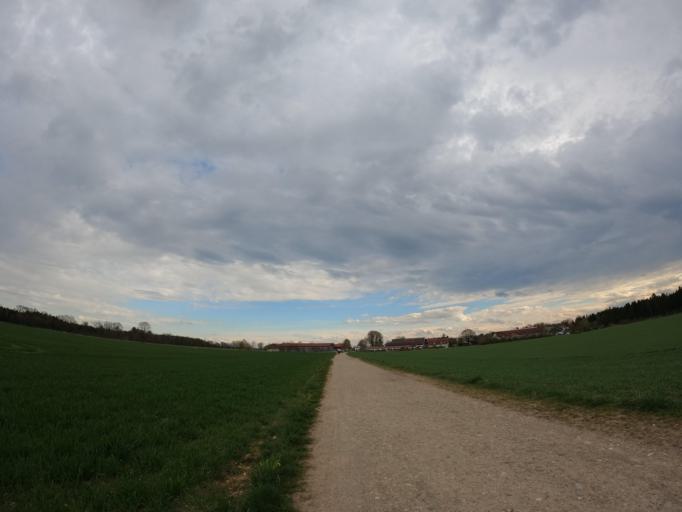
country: DE
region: Bavaria
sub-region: Upper Bavaria
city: Putzbrunn
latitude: 48.0953
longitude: 11.7061
